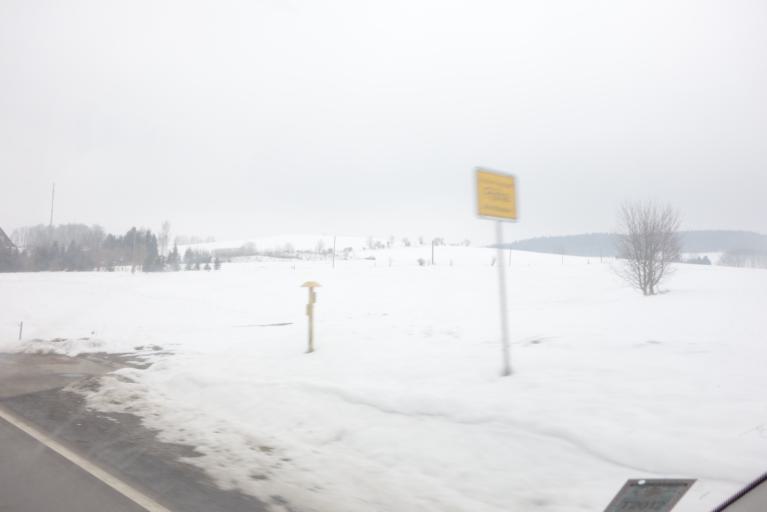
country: DE
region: Saxony
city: Floha
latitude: 50.8590
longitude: 13.0936
